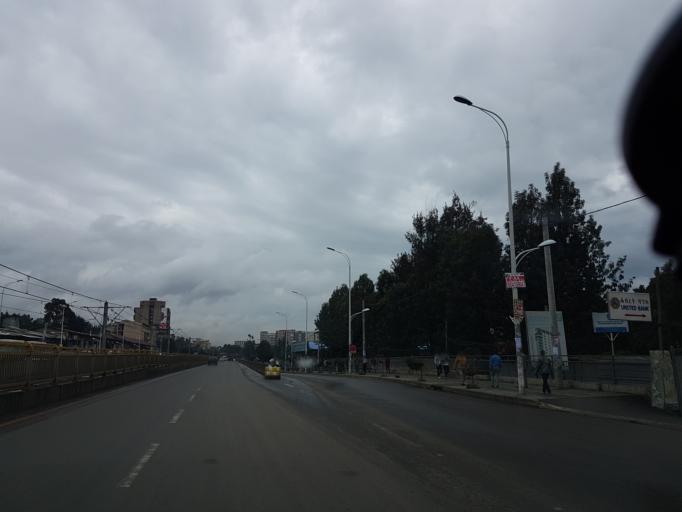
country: ET
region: Adis Abeba
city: Addis Ababa
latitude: 9.0198
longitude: 38.8042
